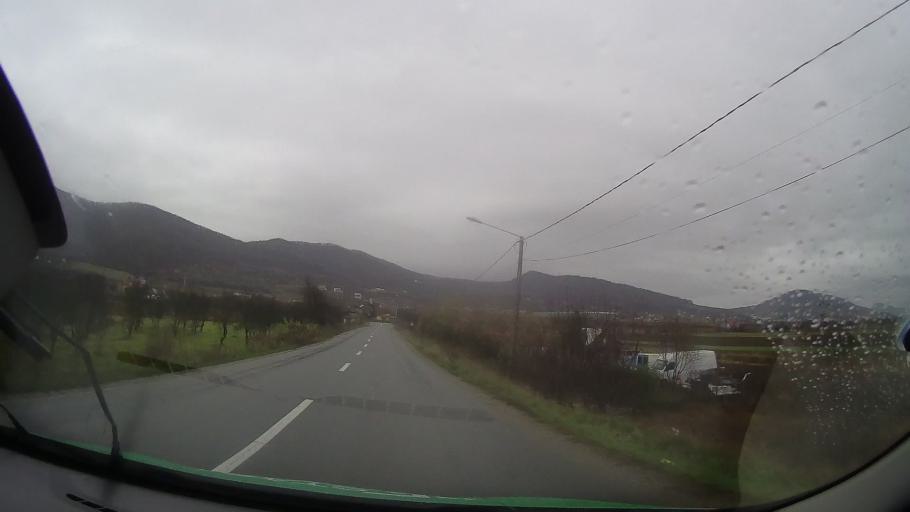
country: RO
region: Bistrita-Nasaud
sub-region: Municipiul Bistrita
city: Viisoara
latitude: 47.0798
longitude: 24.4365
